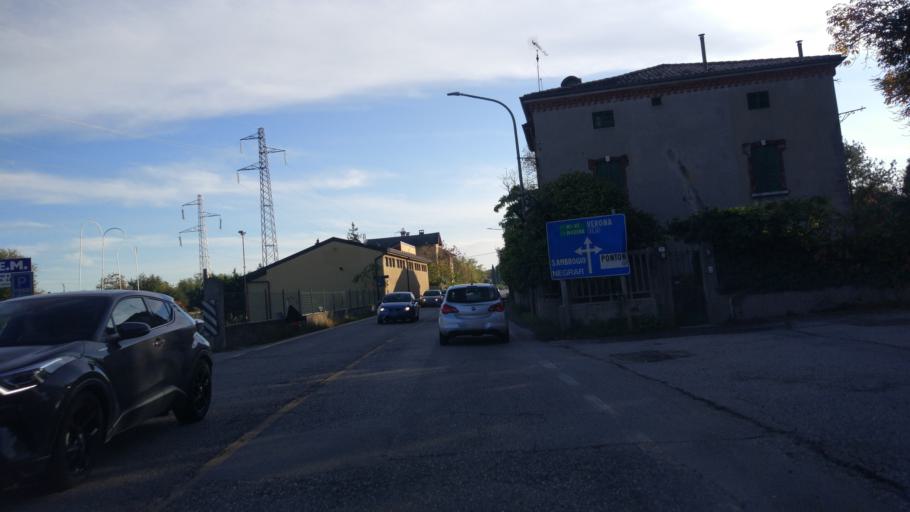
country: IT
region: Veneto
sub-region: Provincia di Verona
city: Volargne
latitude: 45.5217
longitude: 10.8187
